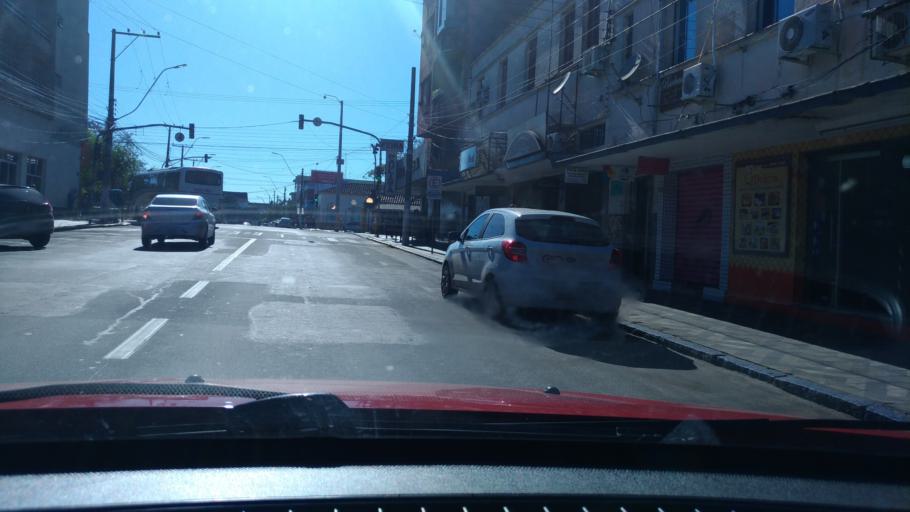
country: BR
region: Rio Grande do Sul
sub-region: Viamao
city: Viamao
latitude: -30.0826
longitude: -51.0275
